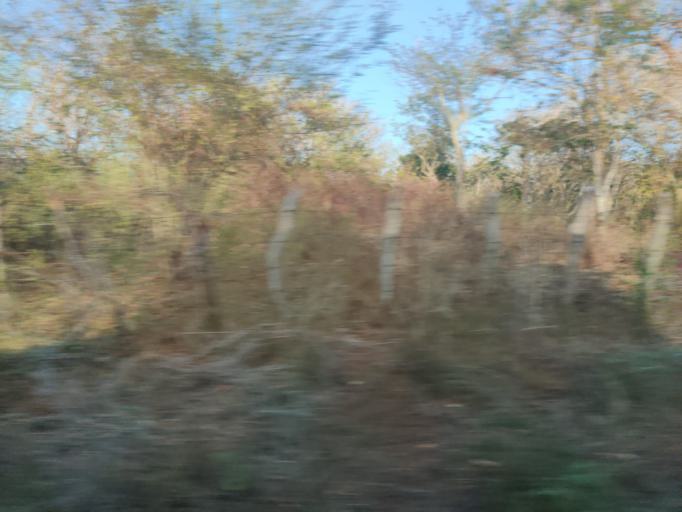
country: CO
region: Atlantico
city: Piojo
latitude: 10.7456
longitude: -75.2445
